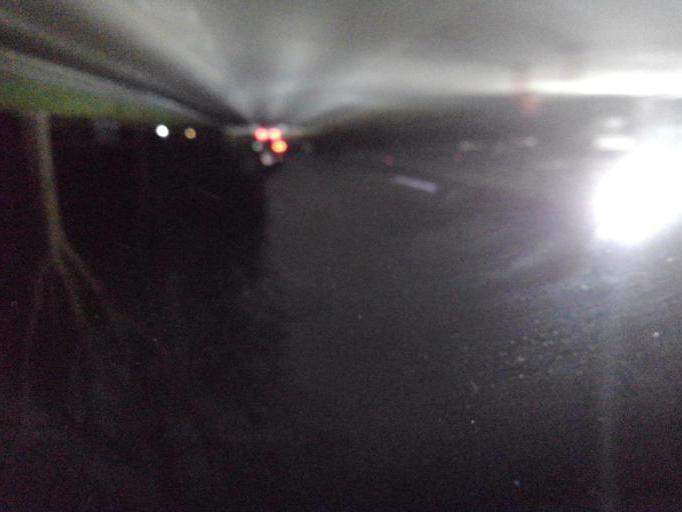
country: JP
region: Saitama
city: Tokorozawa
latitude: 35.8089
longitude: 139.4671
